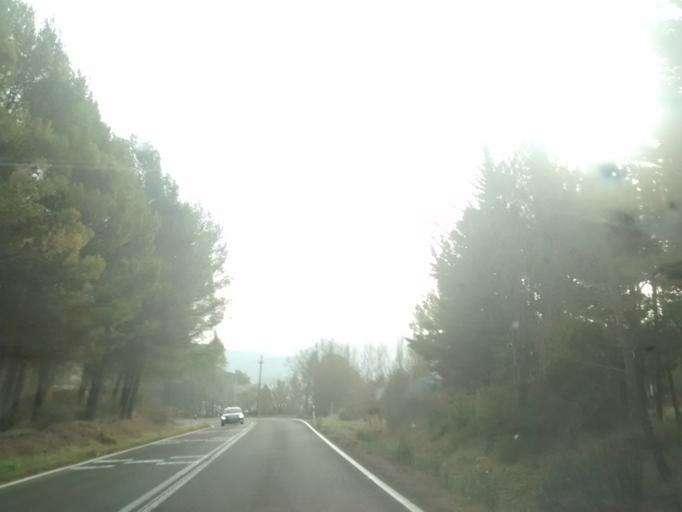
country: ES
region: Aragon
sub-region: Provincia de Zaragoza
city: Undues de Lerda
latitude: 42.6171
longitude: -1.1141
